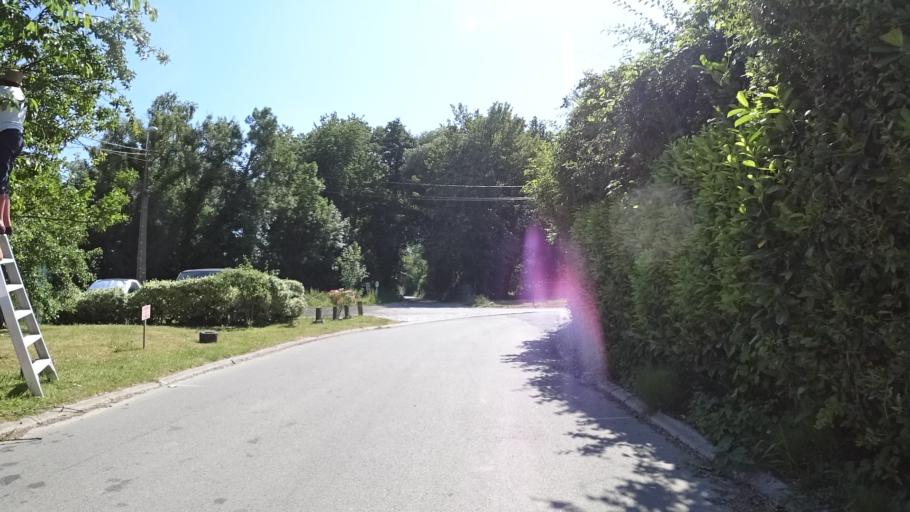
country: BE
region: Wallonia
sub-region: Province du Brabant Wallon
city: Incourt
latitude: 50.6974
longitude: 4.8224
